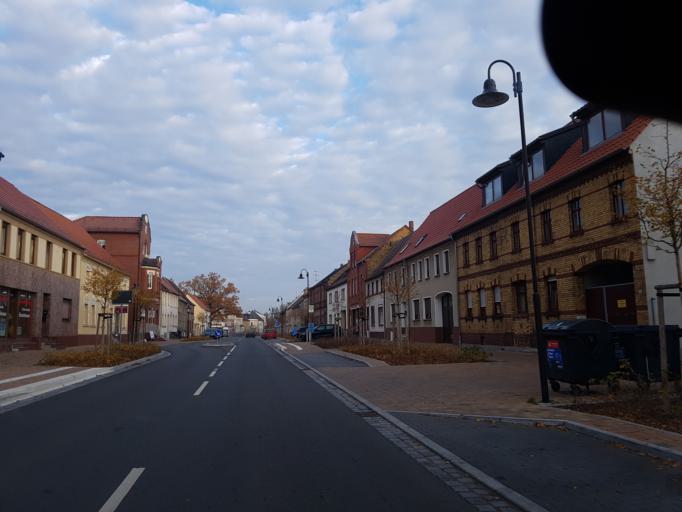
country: DE
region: Saxony-Anhalt
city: Zahna
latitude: 51.9125
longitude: 12.7869
